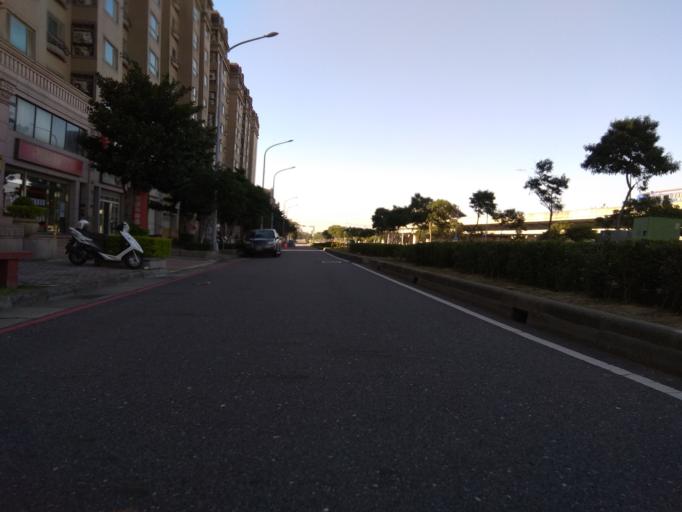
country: TW
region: Taiwan
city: Taoyuan City
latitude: 25.0223
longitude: 121.2225
